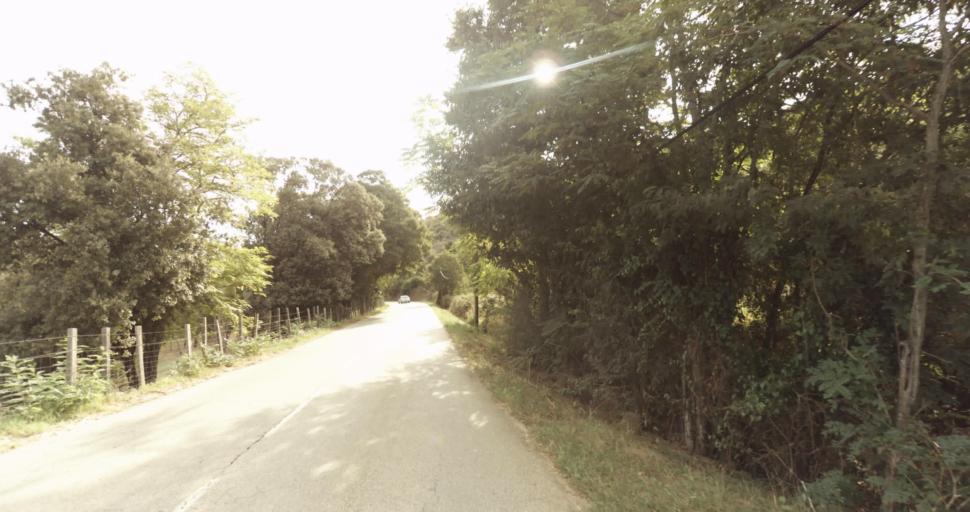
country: FR
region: Corsica
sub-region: Departement de la Corse-du-Sud
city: Ajaccio
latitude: 41.9290
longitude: 8.7046
